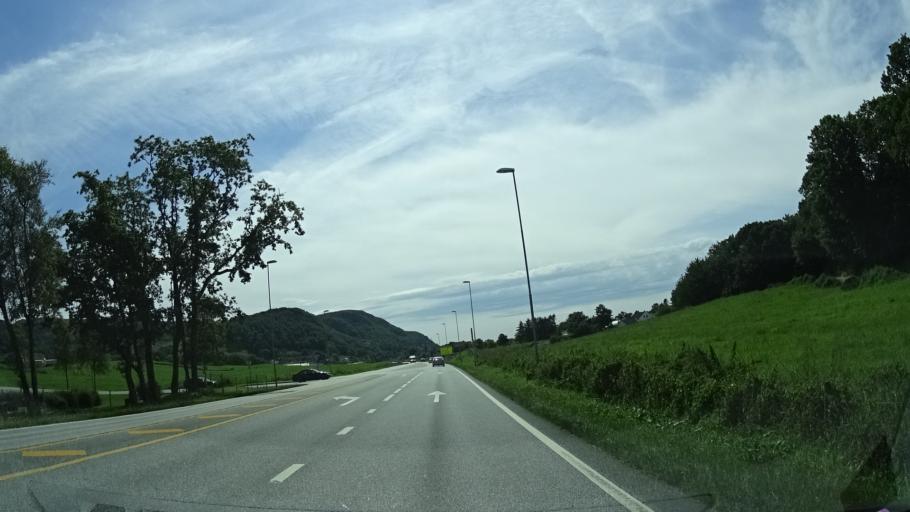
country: NO
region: Rogaland
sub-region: Rennesoy
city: Vikevag
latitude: 59.1151
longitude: 5.6974
